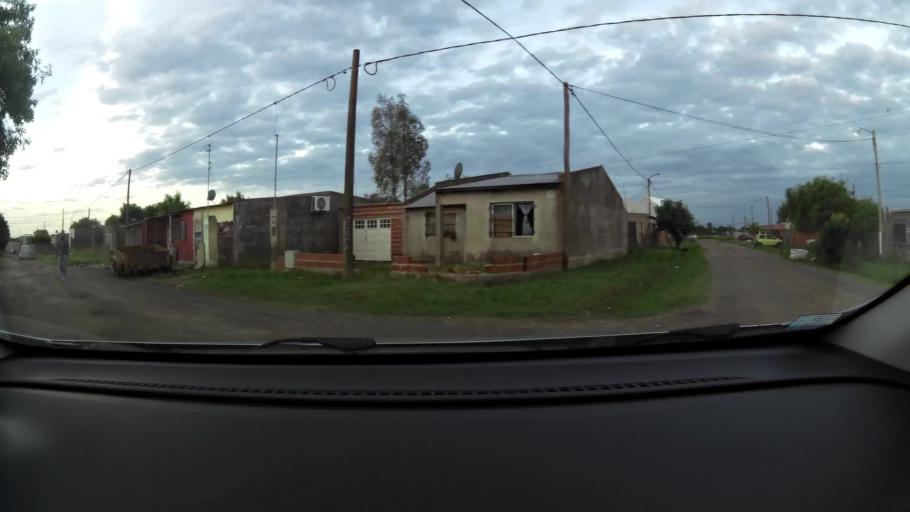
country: AR
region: Buenos Aires
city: San Nicolas de los Arroyos
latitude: -33.3171
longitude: -60.2472
